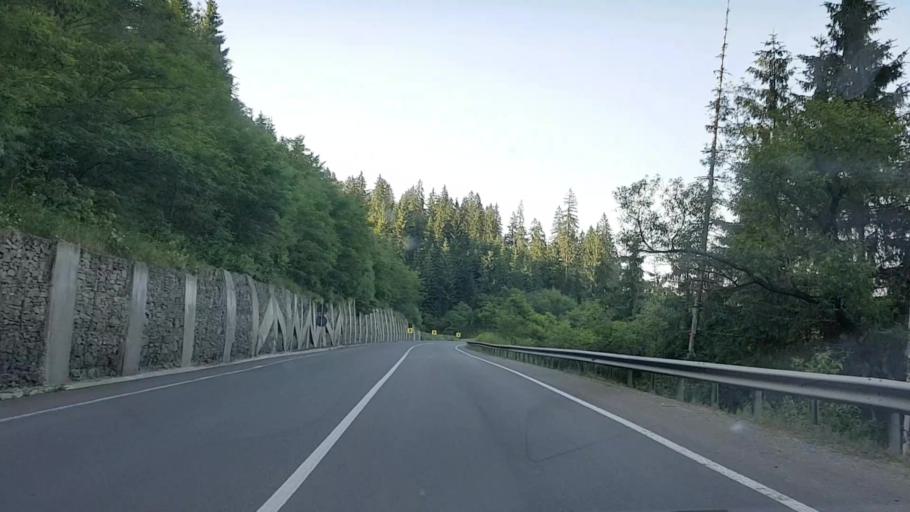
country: RO
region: Bistrita-Nasaud
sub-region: Comuna Lunca Ilvei
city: Lunca Ilvei
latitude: 47.2262
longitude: 24.9615
